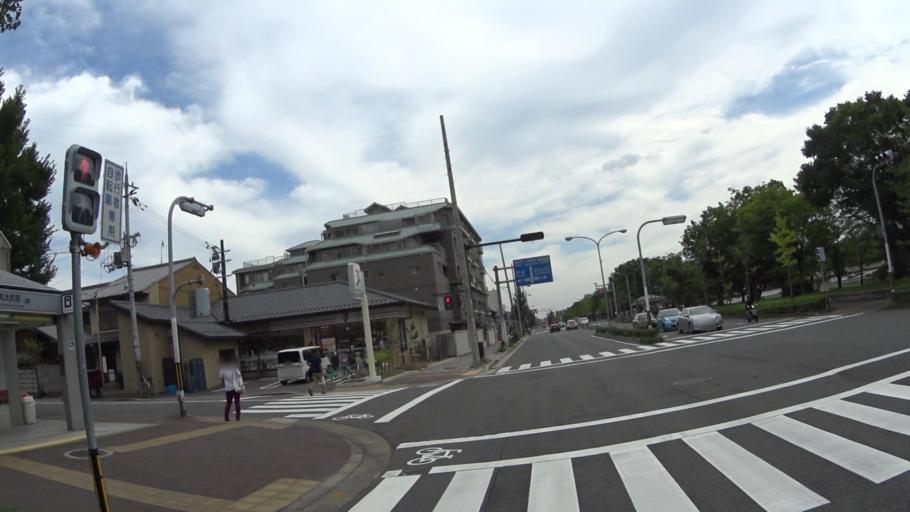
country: JP
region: Kyoto
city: Kyoto
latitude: 35.0188
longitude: 135.7722
